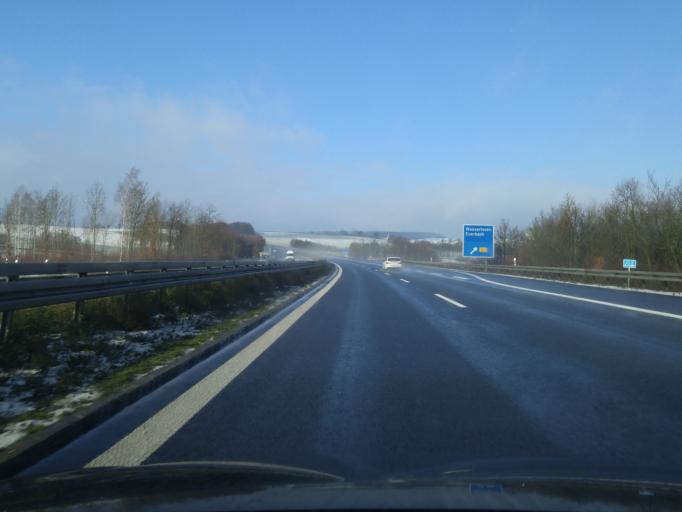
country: DE
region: Bavaria
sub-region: Regierungsbezirk Unterfranken
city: Wasserlosen
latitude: 50.0634
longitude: 10.0482
